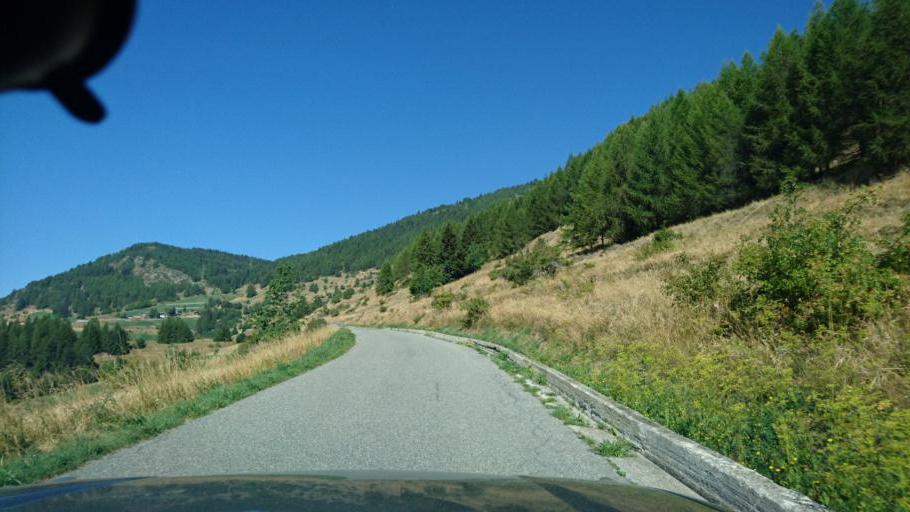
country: IT
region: Aosta Valley
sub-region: Valle d'Aosta
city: Saint-Nicolas
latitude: 45.7246
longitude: 7.1525
